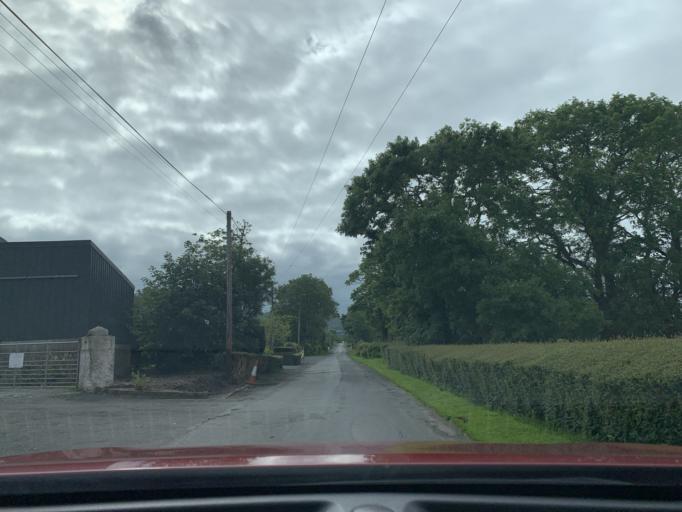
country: IE
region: Connaught
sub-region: Sligo
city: Sligo
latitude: 54.3411
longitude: -8.4831
